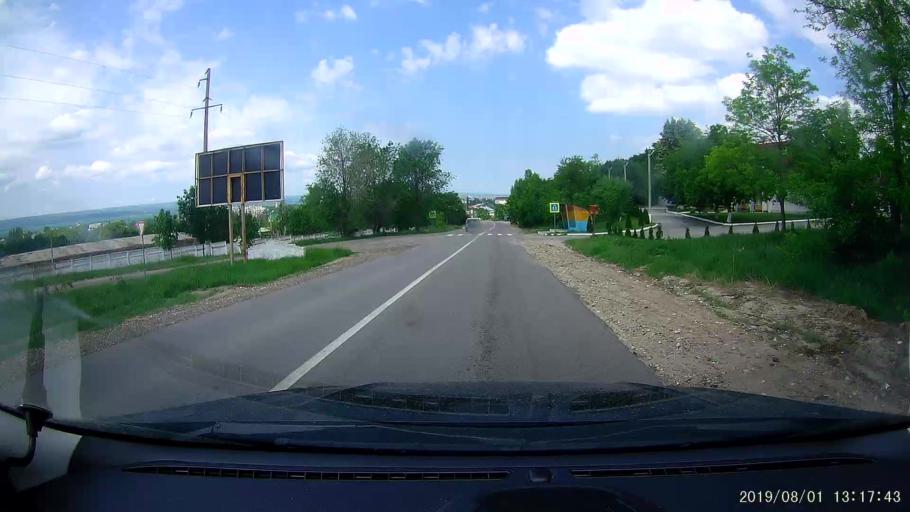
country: MD
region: Cahul
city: Cahul
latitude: 45.8914
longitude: 28.2081
